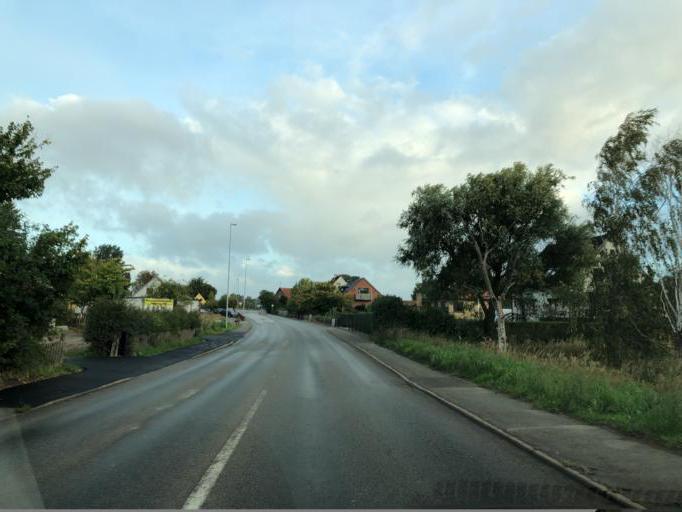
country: SE
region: Skane
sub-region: Landskrona
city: Asmundtorp
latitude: 55.8586
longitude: 12.9019
